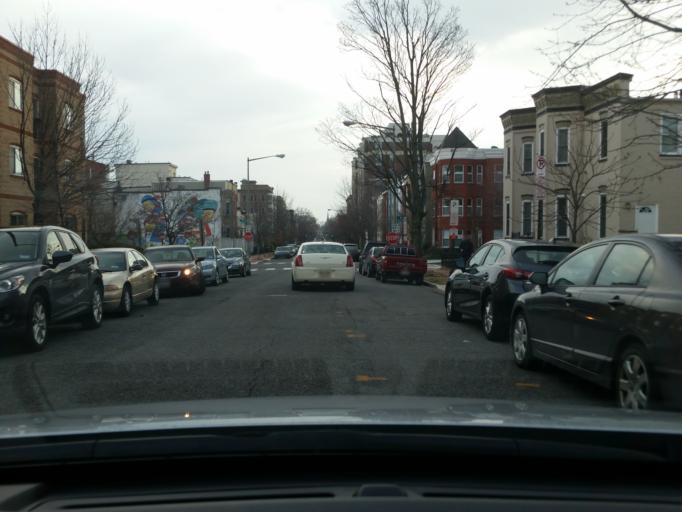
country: US
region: Washington, D.C.
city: Washington, D.C.
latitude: 38.9197
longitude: -77.0281
